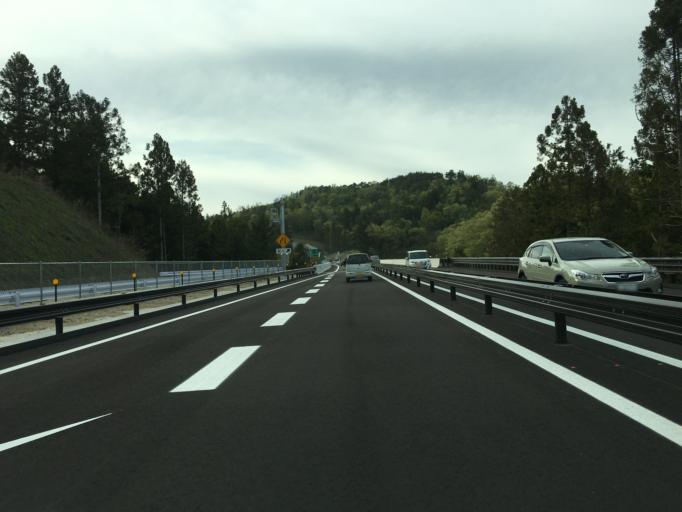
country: JP
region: Fukushima
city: Hobaramachi
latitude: 37.7750
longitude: 140.5829
